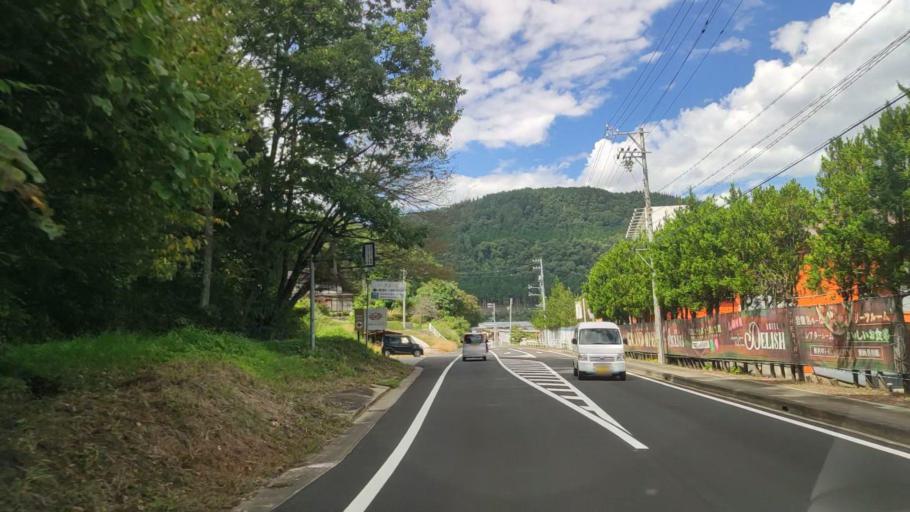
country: JP
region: Gifu
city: Takayama
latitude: 36.1835
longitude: 137.2568
